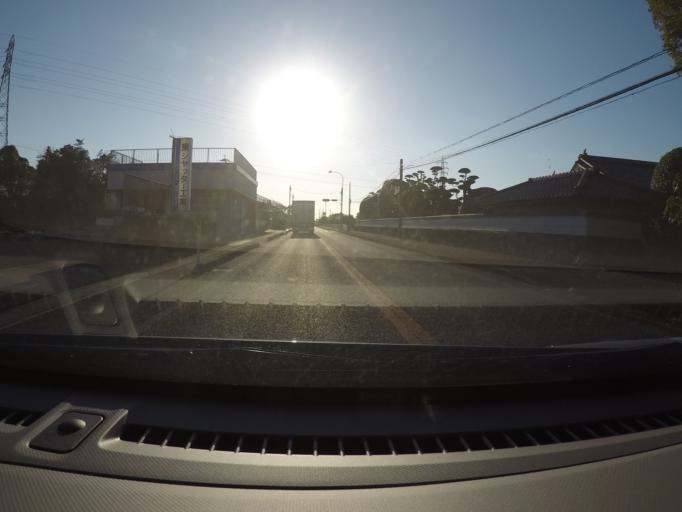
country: JP
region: Kagoshima
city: Izumi
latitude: 32.0953
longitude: 130.2990
